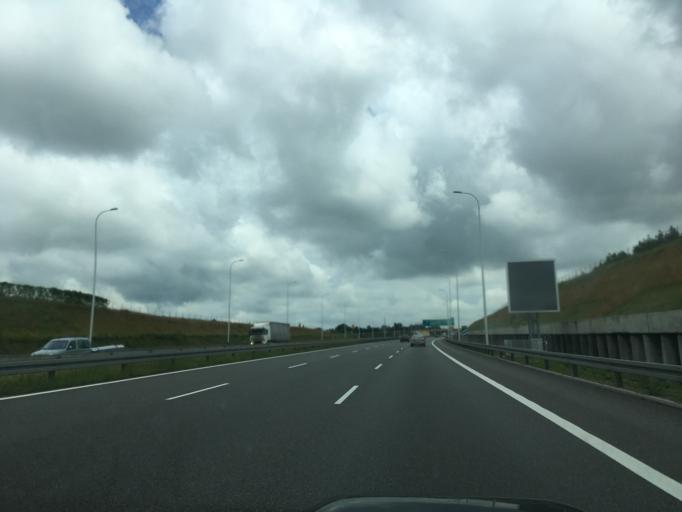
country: PL
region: Lublin Voivodeship
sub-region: Powiat lubelski
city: Jastkow
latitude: 51.3015
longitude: 22.5079
